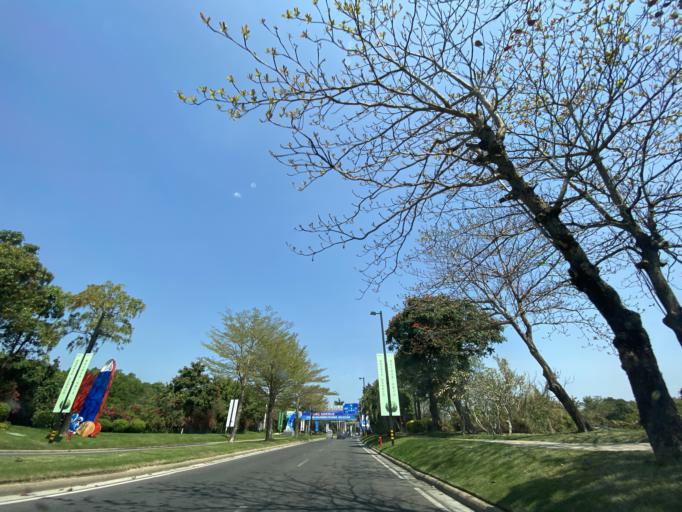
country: CN
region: Hainan
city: Yingzhou
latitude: 18.4216
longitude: 109.8449
